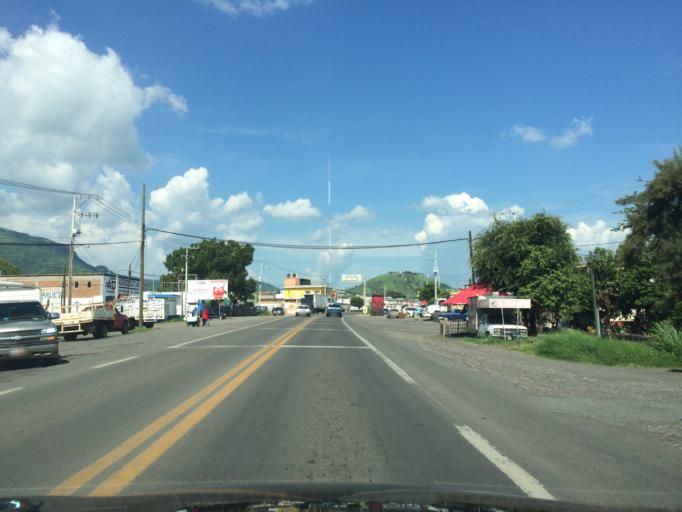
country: MX
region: Nayarit
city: Ixtlan del Rio
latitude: 21.0377
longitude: -104.3818
